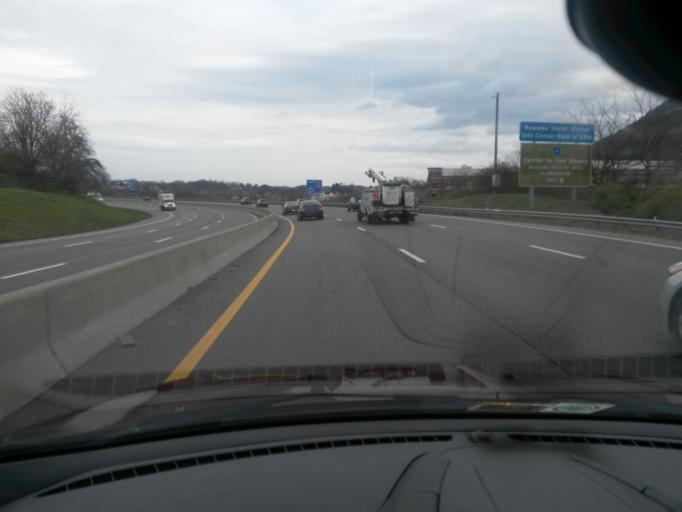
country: US
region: Virginia
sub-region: City of Roanoke
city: Cedar Bluff
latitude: 37.2582
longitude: -79.9453
